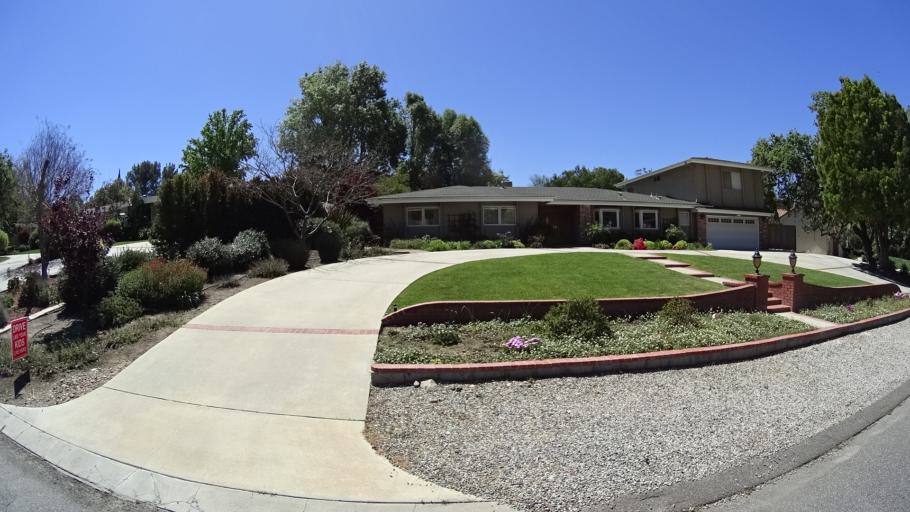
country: US
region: California
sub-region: Ventura County
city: Thousand Oaks
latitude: 34.1937
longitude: -118.8506
